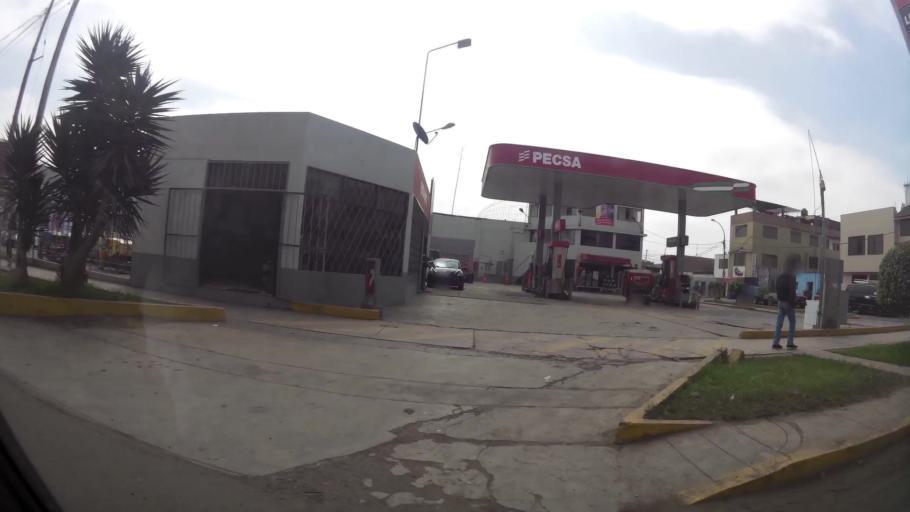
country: PE
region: Lima
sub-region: Provincia de Huaral
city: Huaral
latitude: -11.4976
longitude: -77.2133
